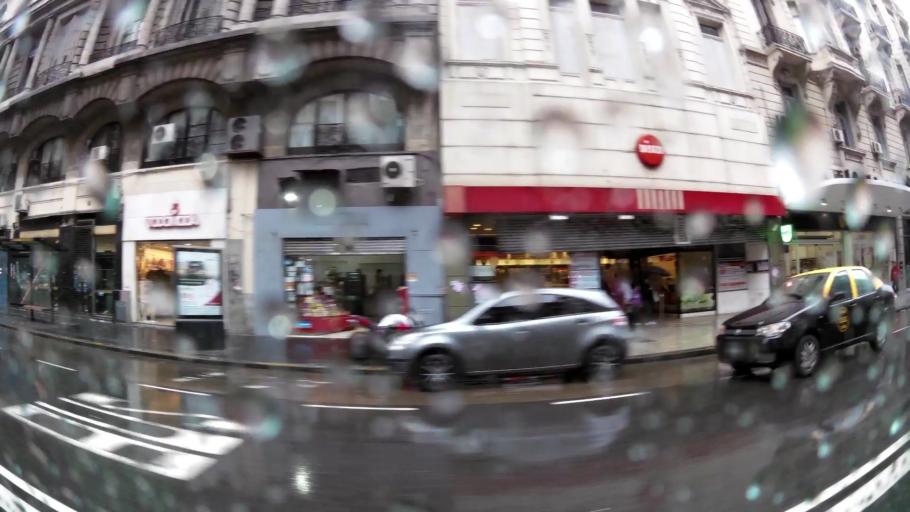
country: AR
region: Buenos Aires F.D.
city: Buenos Aires
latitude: -34.6085
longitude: -58.3920
